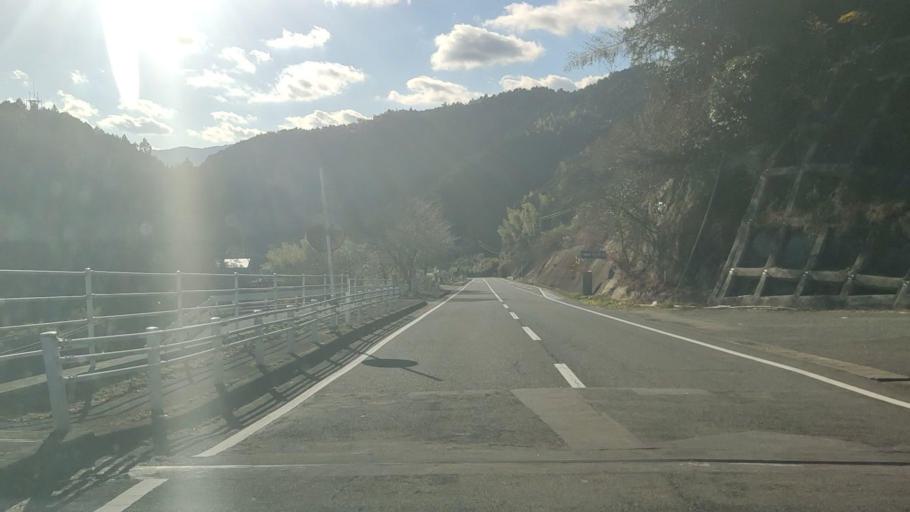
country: JP
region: Saga Prefecture
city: Kanzakimachi-kanzaki
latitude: 33.3890
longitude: 130.2645
